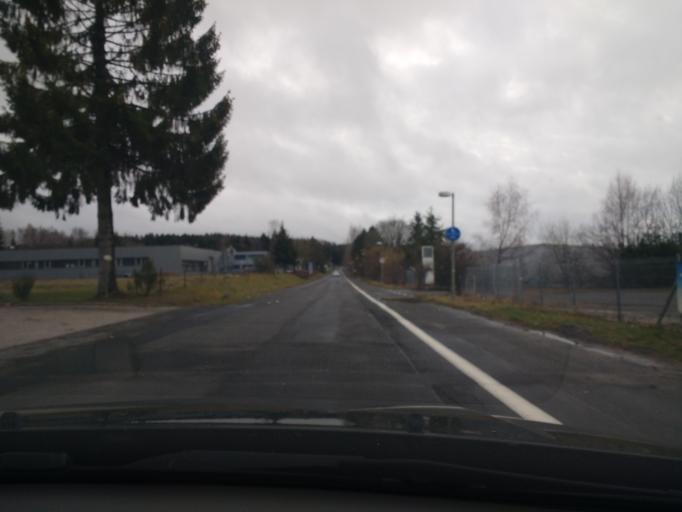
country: DE
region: Rheinland-Pfalz
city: Damflos
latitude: 49.6733
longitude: 6.9702
